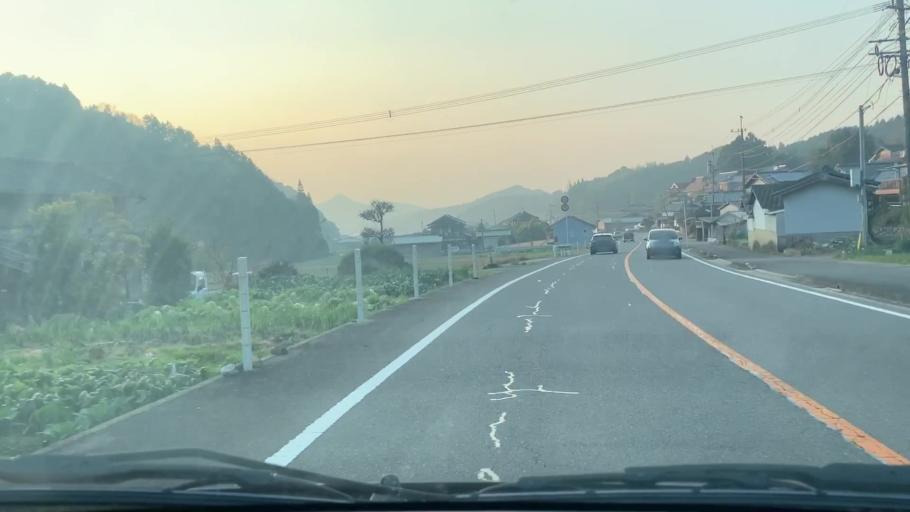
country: JP
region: Saga Prefecture
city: Takeocho-takeo
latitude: 33.2557
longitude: 130.0115
